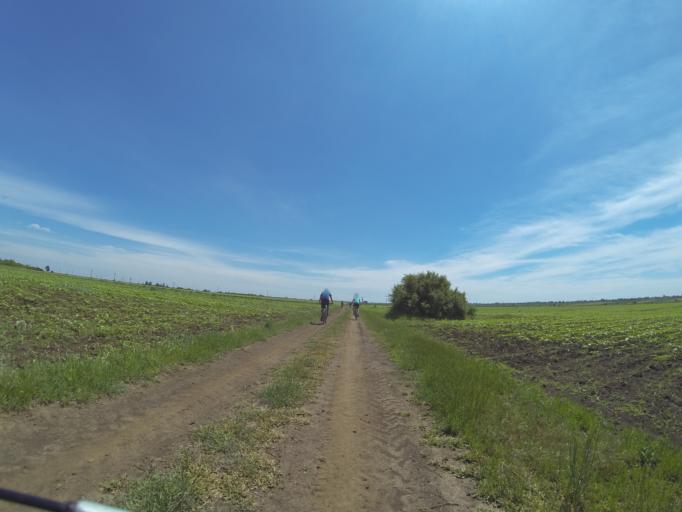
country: RO
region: Dolj
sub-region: Comuna Leu
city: Zanoaga
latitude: 44.1765
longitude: 24.0880
